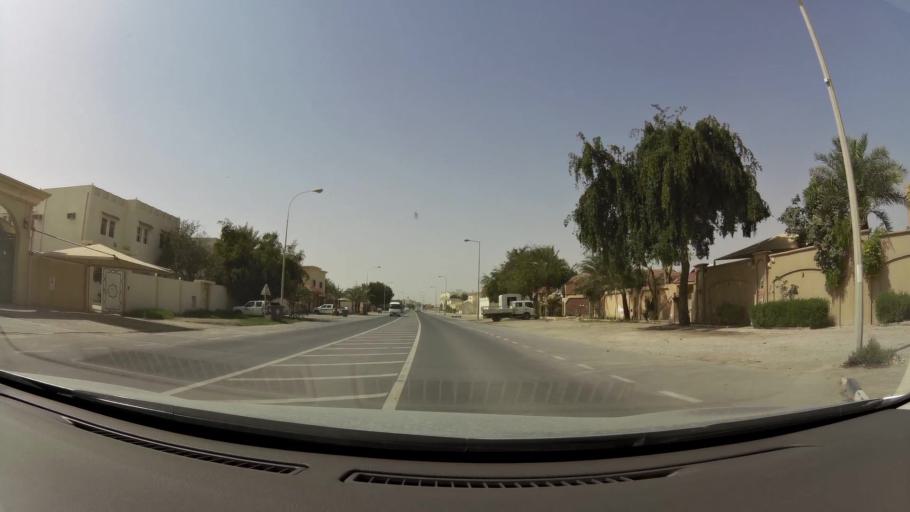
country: QA
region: Baladiyat Umm Salal
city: Umm Salal Muhammad
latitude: 25.3914
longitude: 51.4298
